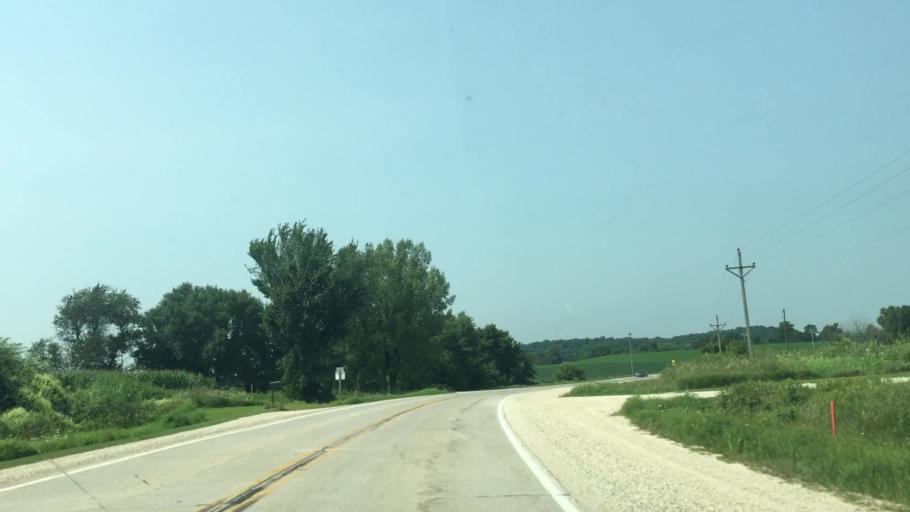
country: US
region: Iowa
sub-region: Fayette County
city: West Union
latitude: 43.0991
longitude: -91.8680
